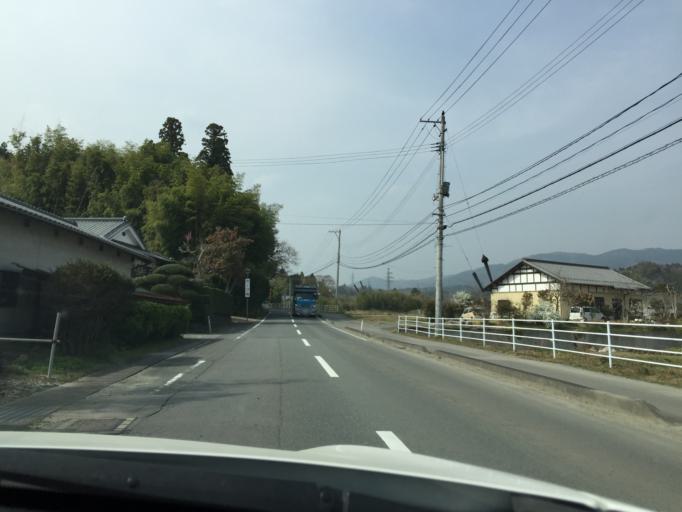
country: JP
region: Fukushima
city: Iwaki
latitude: 37.0157
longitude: 140.7366
